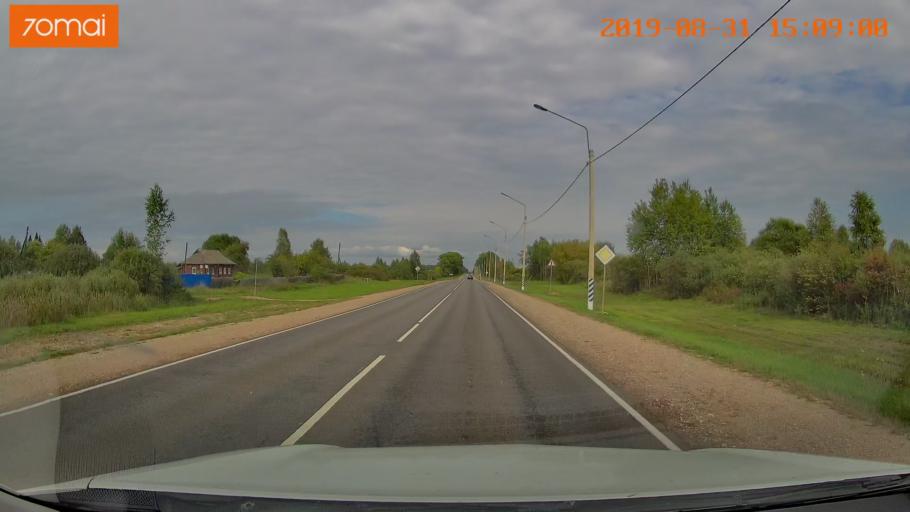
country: RU
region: Kaluga
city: Spas-Demensk
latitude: 54.3972
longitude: 34.1930
